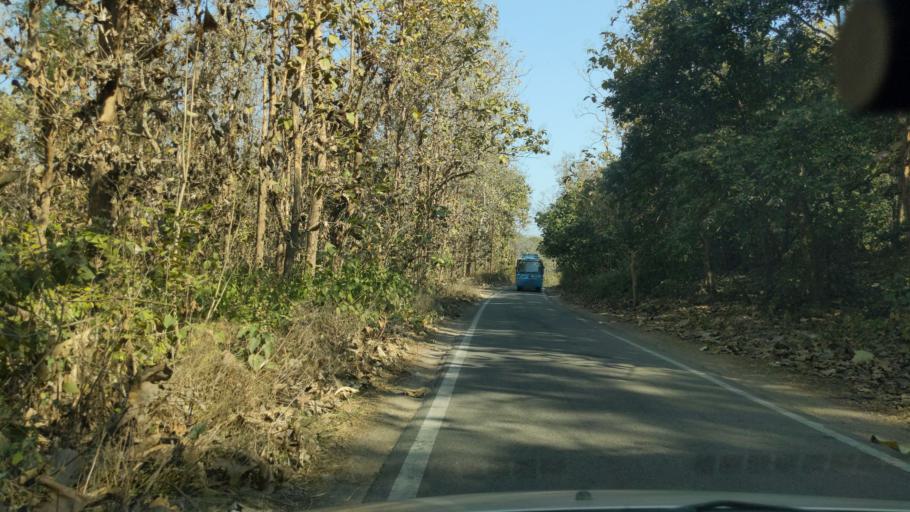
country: IN
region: Uttarakhand
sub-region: Naini Tal
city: Ramnagar
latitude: 29.4053
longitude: 79.1372
